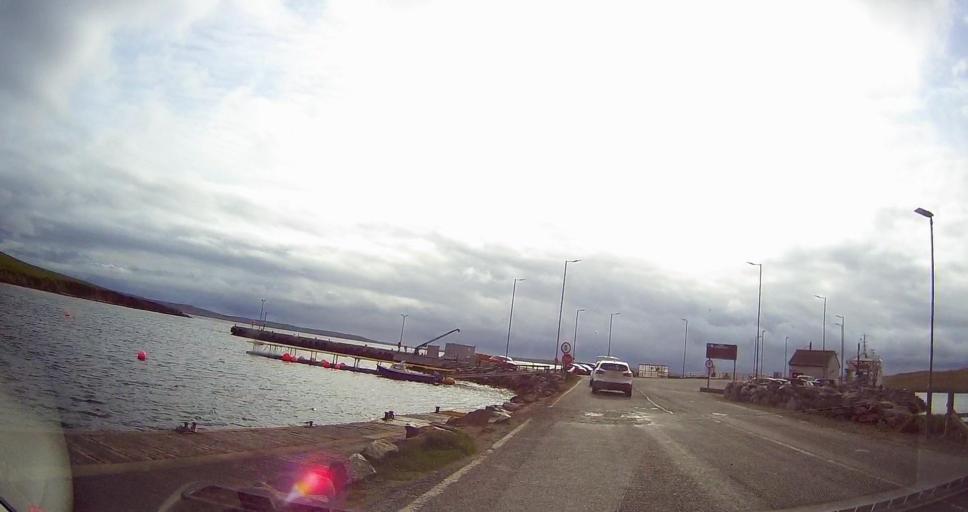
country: GB
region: Scotland
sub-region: Shetland Islands
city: Lerwick
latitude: 60.4667
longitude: -1.2086
